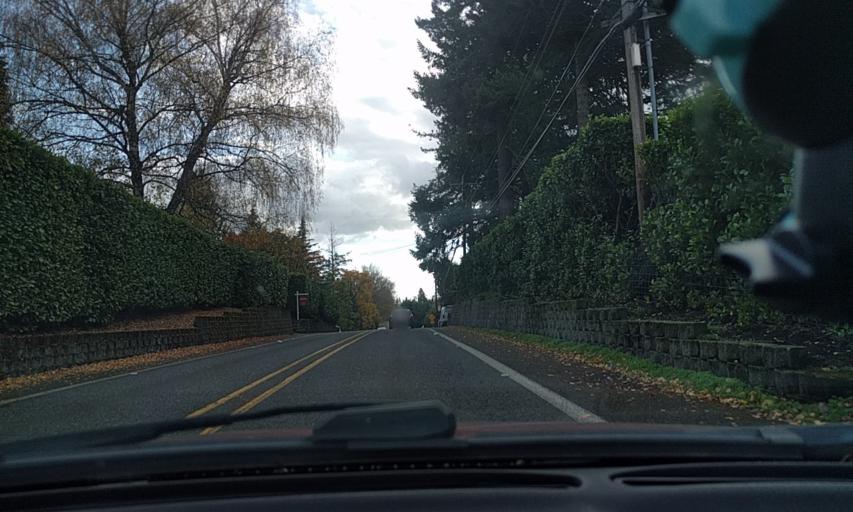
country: US
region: Oregon
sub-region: Washington County
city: West Slope
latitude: 45.4918
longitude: -122.7708
